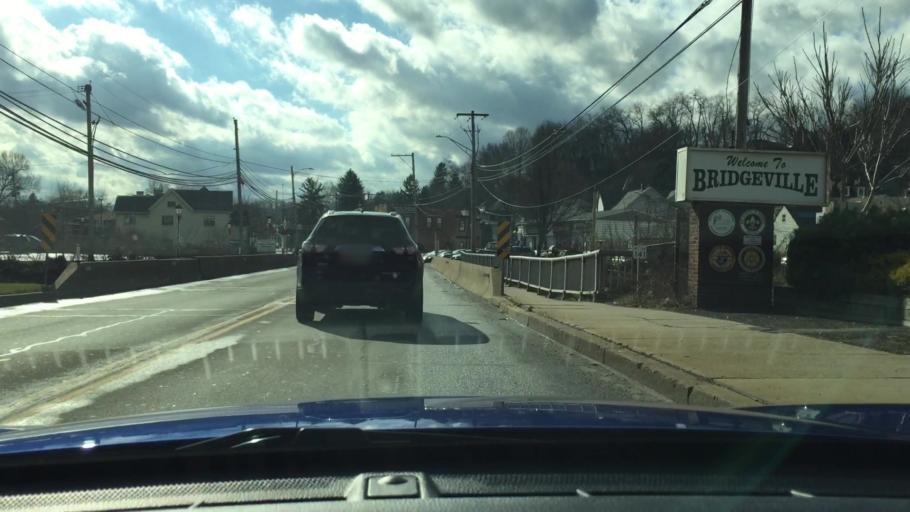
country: US
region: Pennsylvania
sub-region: Allegheny County
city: Bridgeville
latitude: 40.3642
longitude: -80.1097
